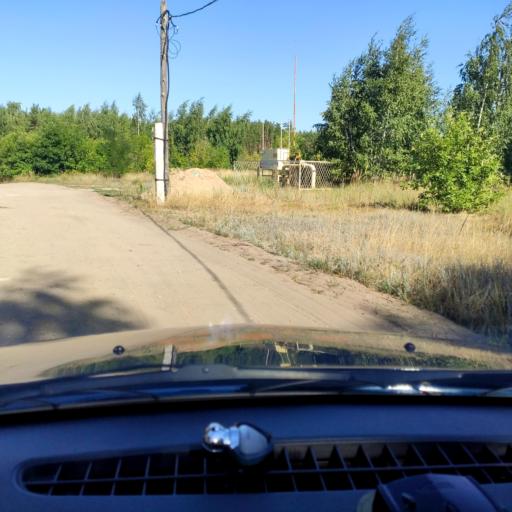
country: RU
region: Voronezj
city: Maslovka
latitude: 51.5435
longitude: 39.1744
